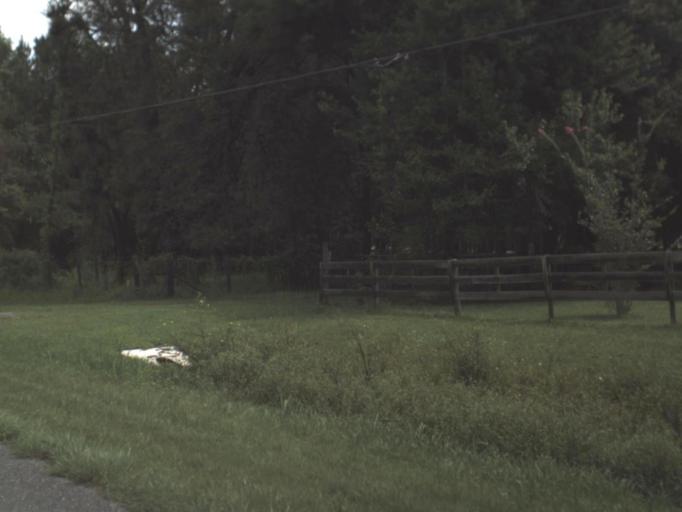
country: US
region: Florida
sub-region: Columbia County
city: Watertown
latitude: 30.0446
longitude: -82.5983
